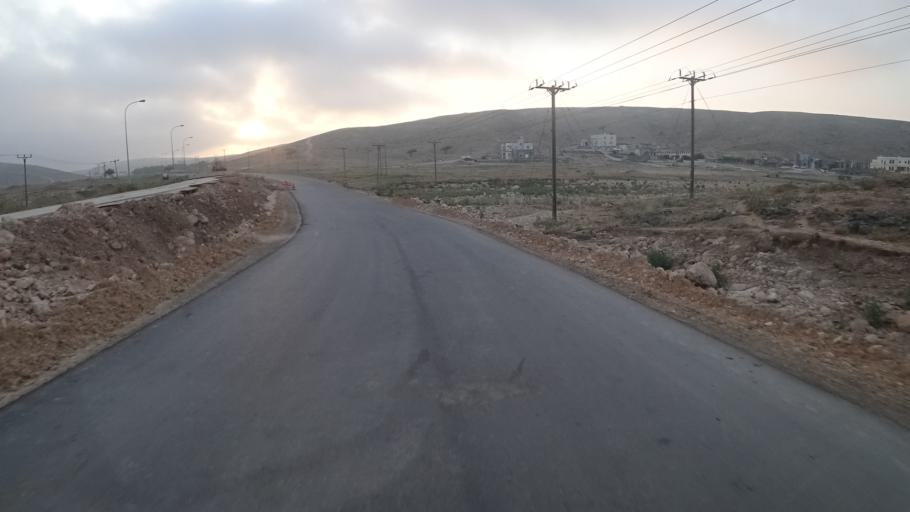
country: OM
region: Zufar
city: Salalah
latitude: 17.1267
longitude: 53.9451
